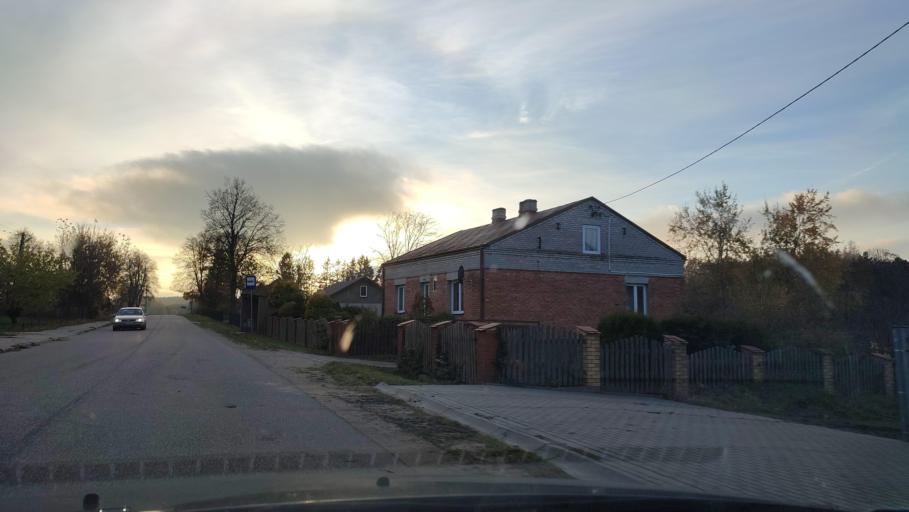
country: PL
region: Masovian Voivodeship
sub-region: Powiat mlawski
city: Wieczfnia Koscielna
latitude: 53.2180
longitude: 20.5137
